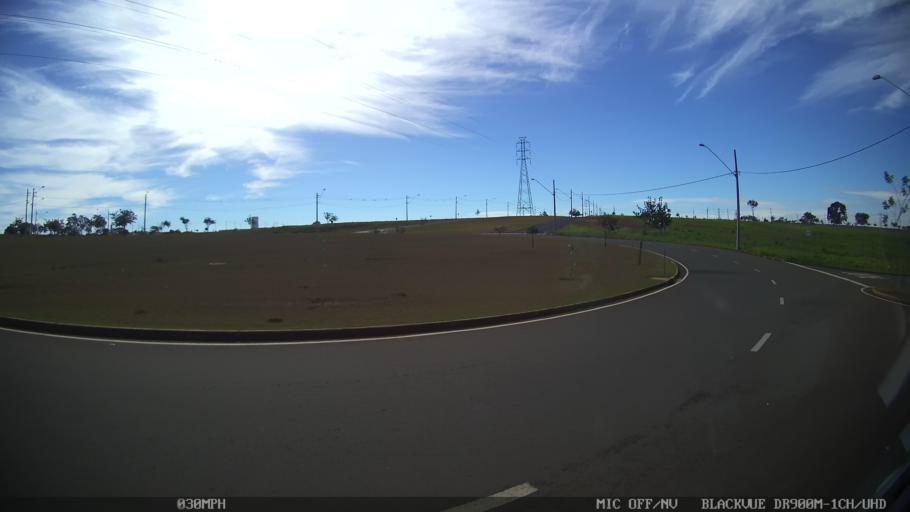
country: BR
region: Sao Paulo
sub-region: Sao Jose Do Rio Preto
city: Sao Jose do Rio Preto
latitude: -20.8561
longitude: -49.3778
